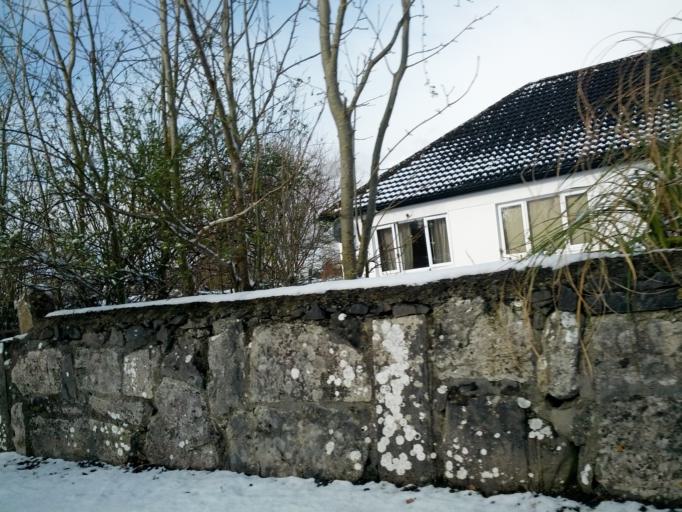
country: IE
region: Connaught
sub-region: County Galway
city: Athenry
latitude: 53.2140
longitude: -8.7589
